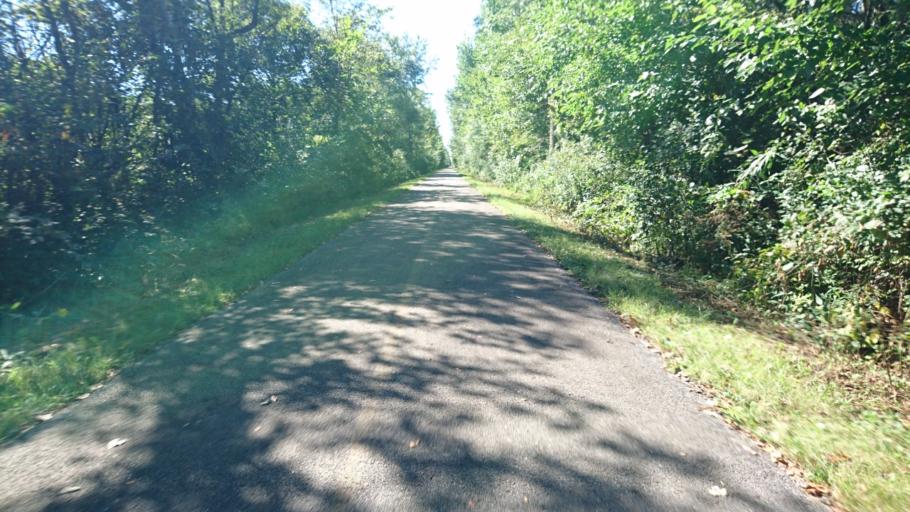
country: US
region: Illinois
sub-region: Cook County
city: Calumet City
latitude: 41.6065
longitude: -87.5494
